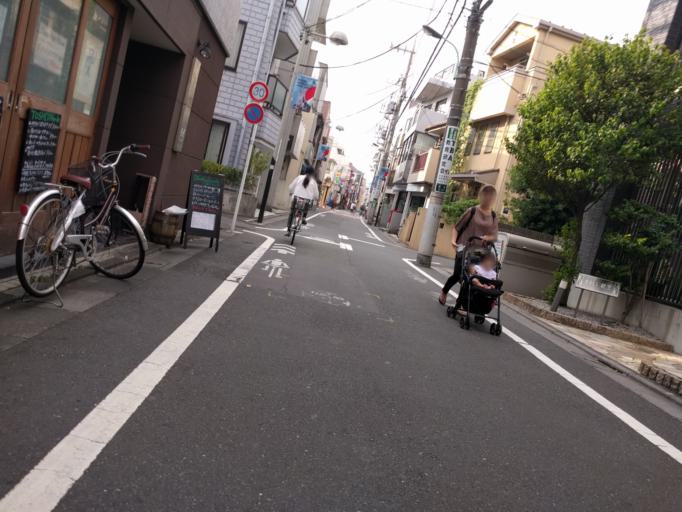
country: JP
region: Tokyo
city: Tokyo
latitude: 35.6539
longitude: 139.6339
